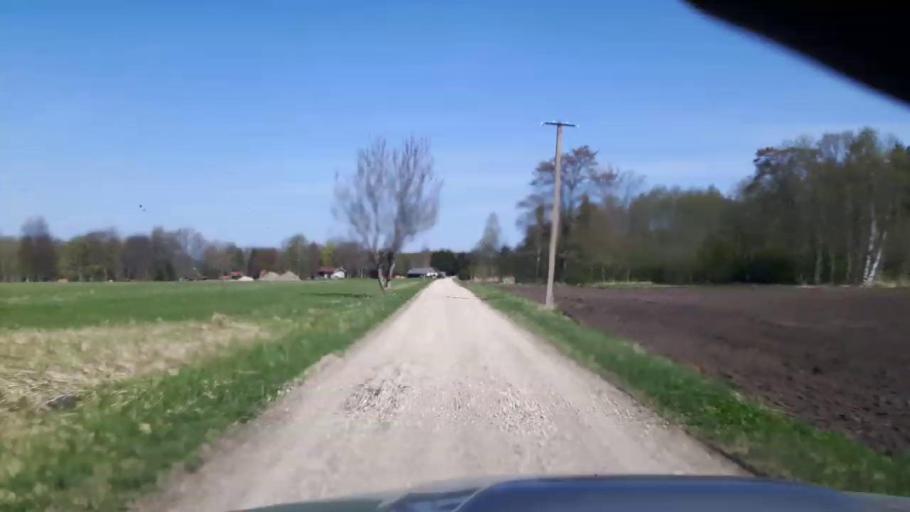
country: EE
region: Paernumaa
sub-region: Tootsi vald
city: Tootsi
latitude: 58.4944
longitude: 24.9303
